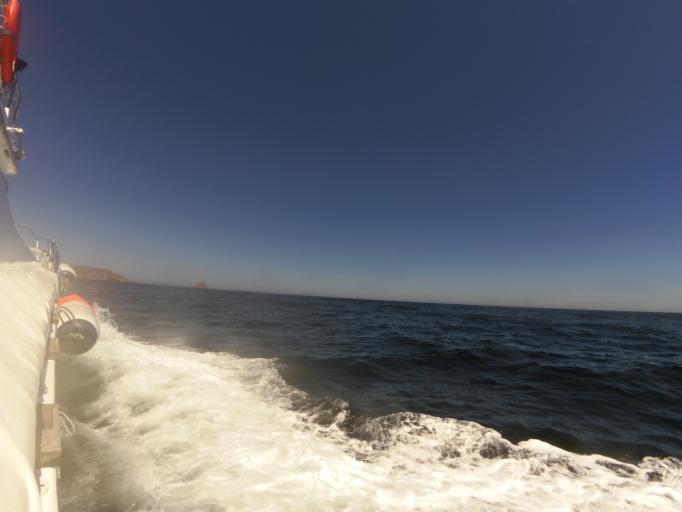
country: PT
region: Leiria
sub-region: Peniche
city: Peniche
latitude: 39.3990
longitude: -9.4853
